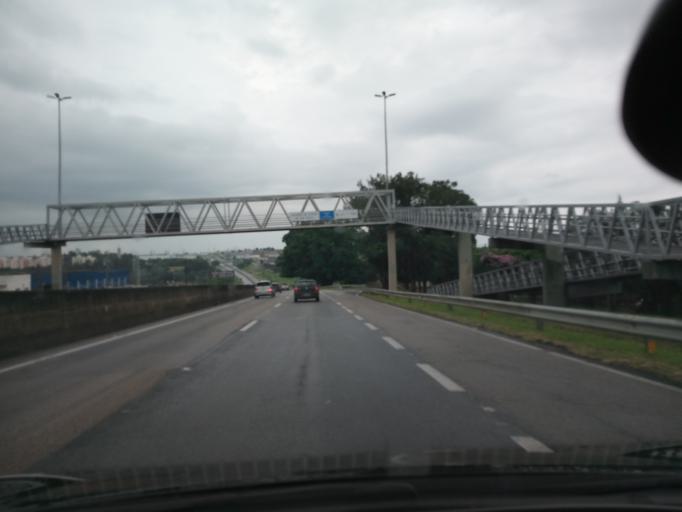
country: BR
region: Sao Paulo
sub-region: Campinas
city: Campinas
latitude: -22.9628
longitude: -47.0983
